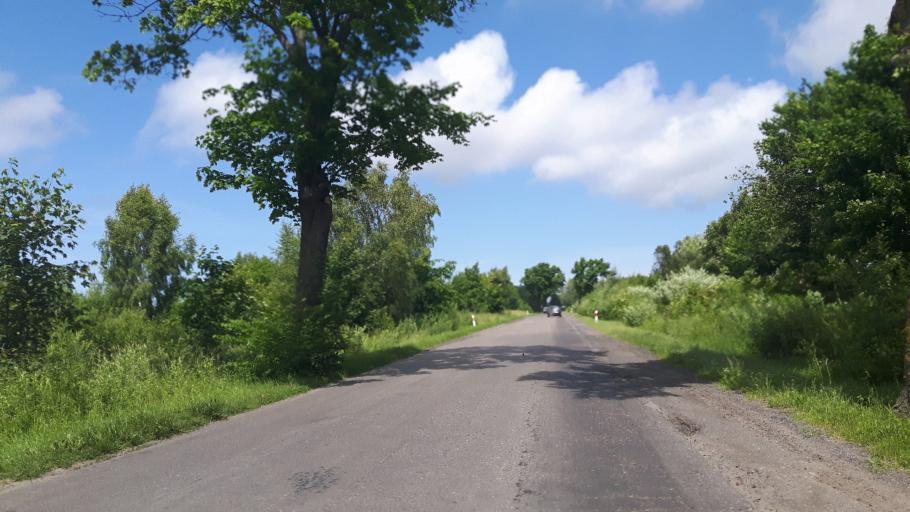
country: PL
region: Pomeranian Voivodeship
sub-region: Powiat slupski
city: Ustka
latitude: 54.5607
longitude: 16.8447
